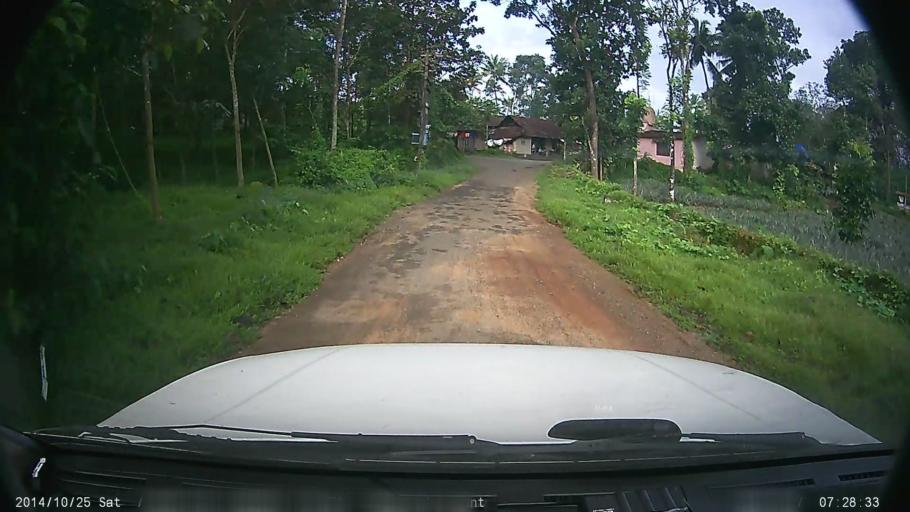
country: IN
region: Kerala
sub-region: Kottayam
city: Palackattumala
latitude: 9.7840
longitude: 76.5632
